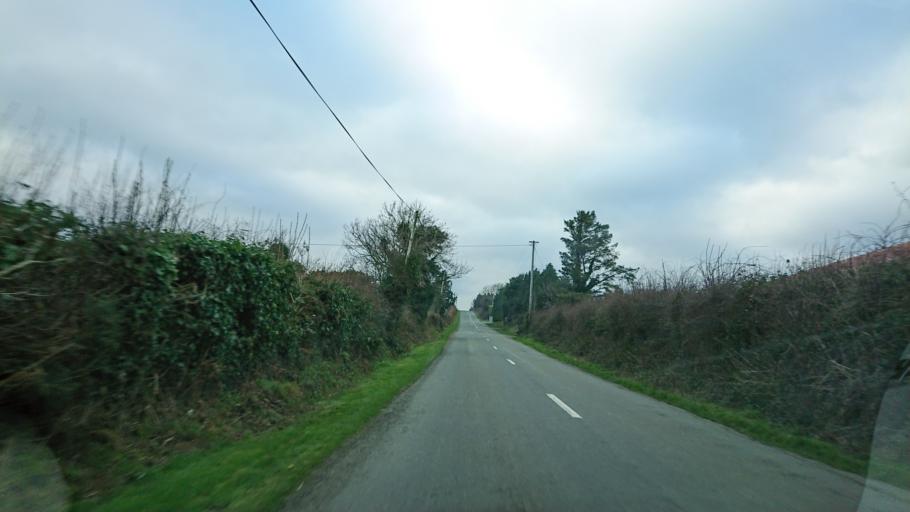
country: IE
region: Munster
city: Carrick-on-Suir
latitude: 52.3195
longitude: -7.5573
